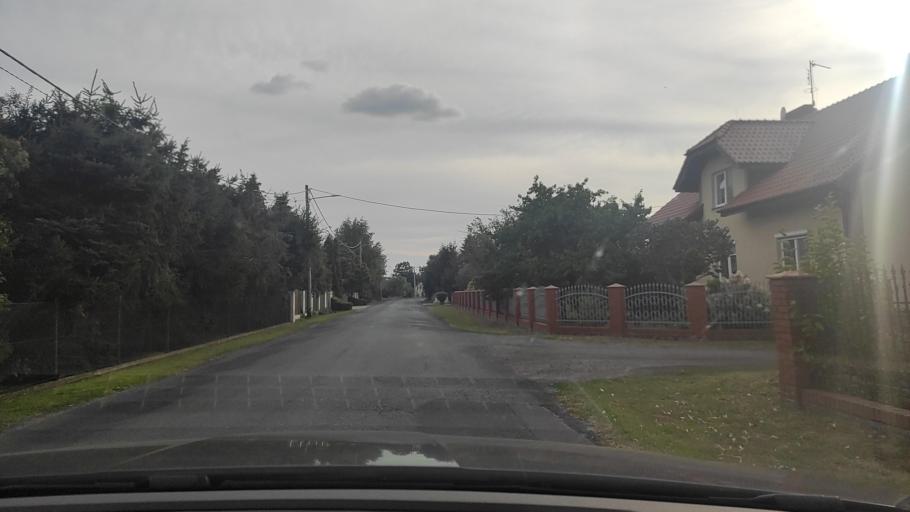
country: PL
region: Greater Poland Voivodeship
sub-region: Powiat poznanski
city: Kleszczewo
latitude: 52.3725
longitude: 17.1549
